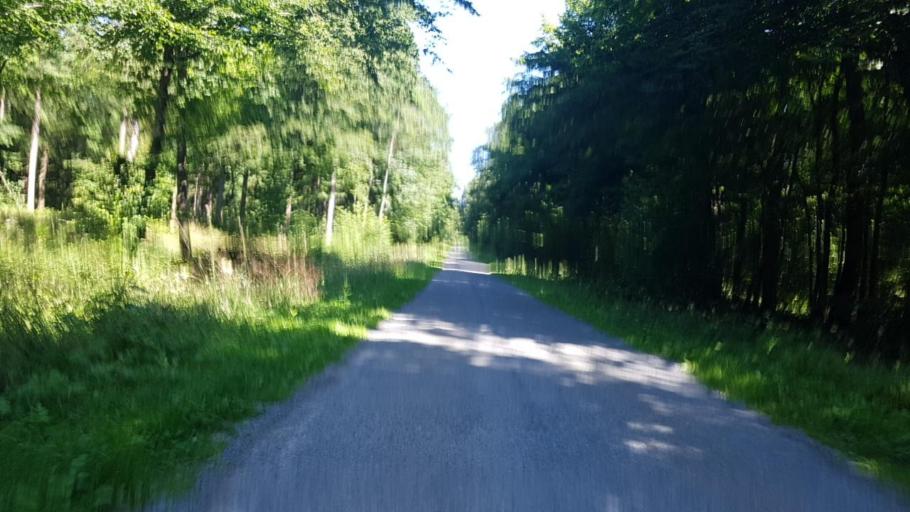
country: BE
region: Wallonia
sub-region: Province du Hainaut
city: Momignies
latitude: 50.0300
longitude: 4.2009
